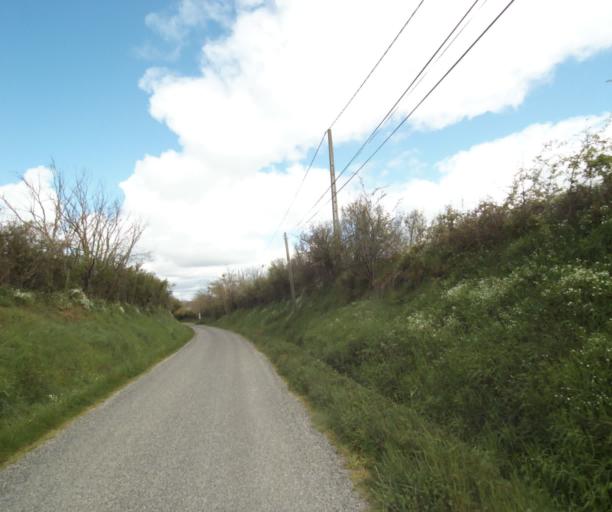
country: FR
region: Midi-Pyrenees
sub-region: Departement de l'Ariege
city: Saverdun
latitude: 43.2251
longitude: 1.5783
